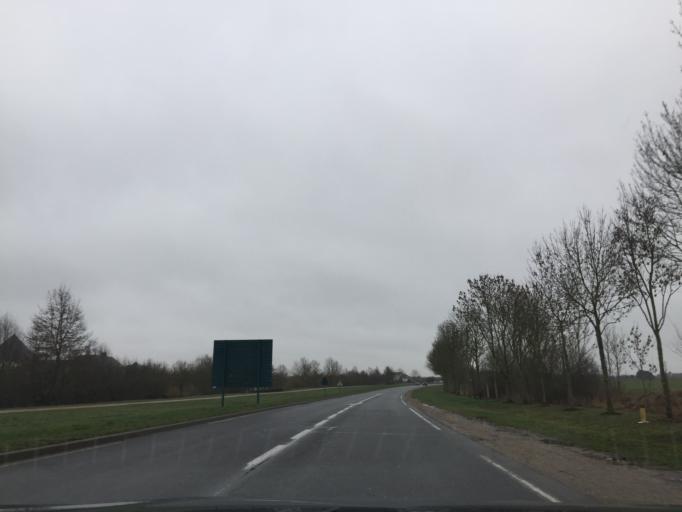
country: FR
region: Ile-de-France
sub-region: Departement de Seine-et-Marne
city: Magny-le-Hongre
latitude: 48.8736
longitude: 2.8036
